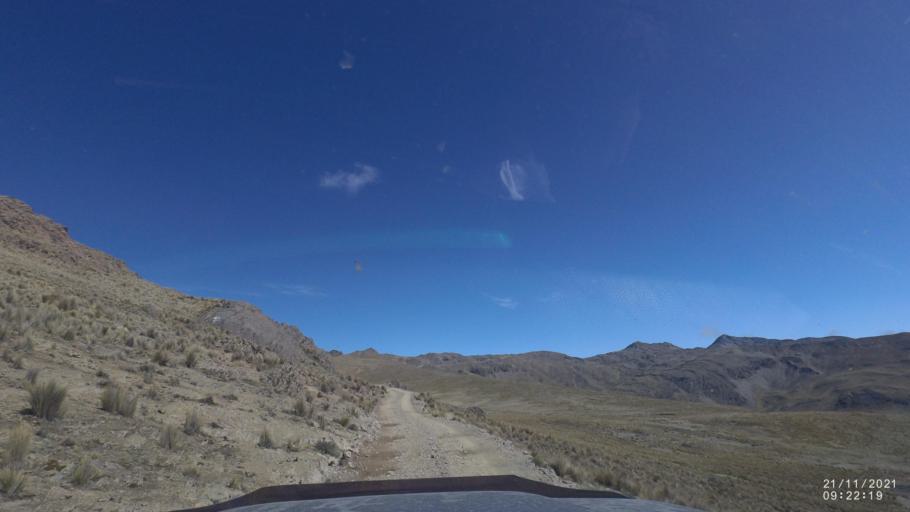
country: BO
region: Cochabamba
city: Cochabamba
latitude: -17.1014
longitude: -66.2482
